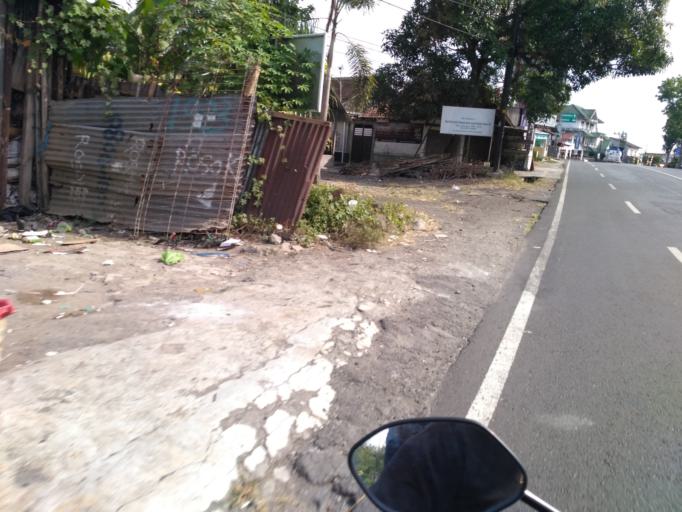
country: ID
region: Daerah Istimewa Yogyakarta
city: Godean
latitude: -7.8117
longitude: 110.2742
